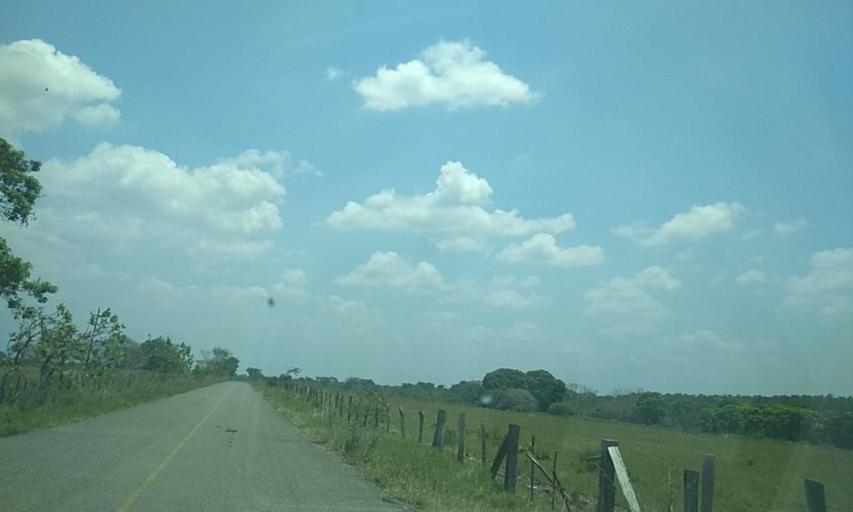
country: MX
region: Tabasco
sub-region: Huimanguillo
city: Francisco Rueda
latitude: 17.8274
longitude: -93.8723
